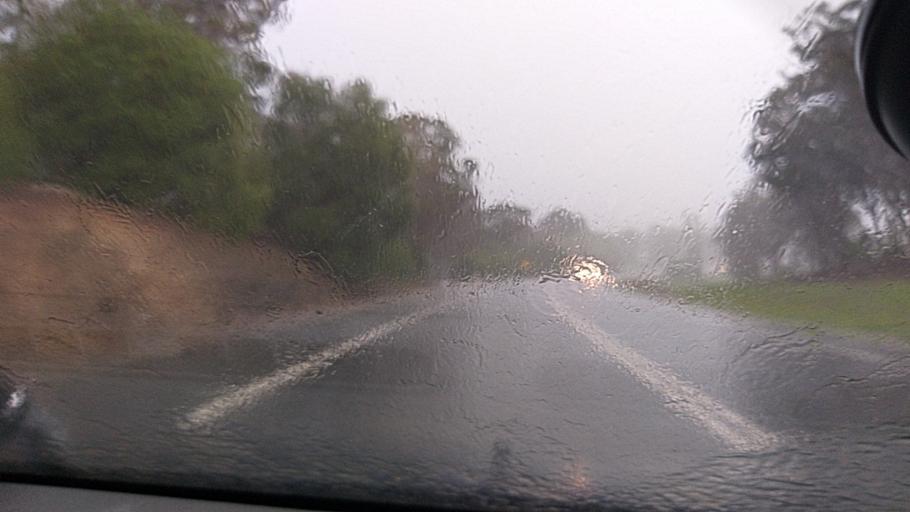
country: AU
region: New South Wales
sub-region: Camden
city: Camden South
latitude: -34.1181
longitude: 150.6987
